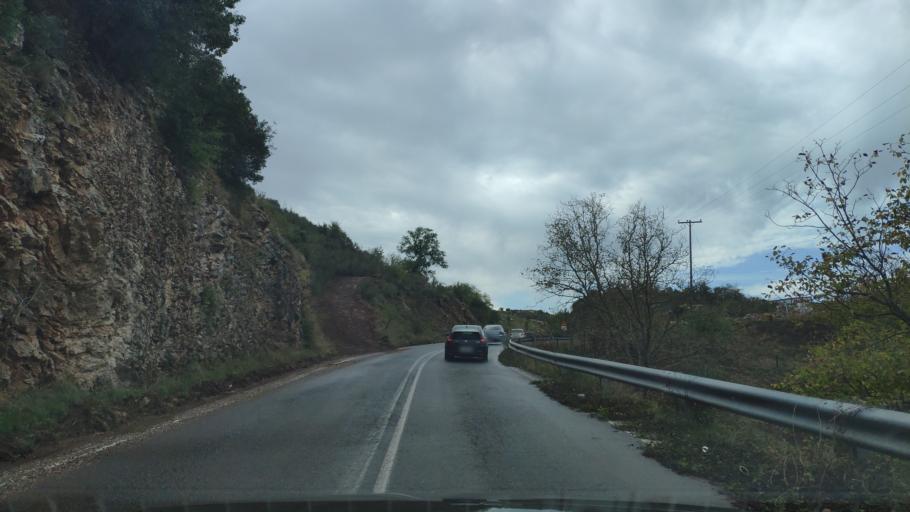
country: GR
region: Peloponnese
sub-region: Nomos Arkadias
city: Dimitsana
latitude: 37.6034
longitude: 22.0403
